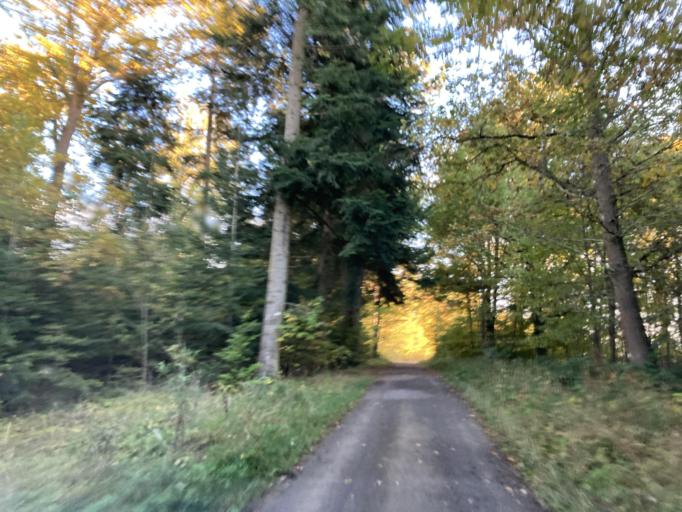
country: DE
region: Baden-Wuerttemberg
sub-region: Regierungsbezirk Stuttgart
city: Motzingen
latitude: 48.5134
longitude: 8.7691
